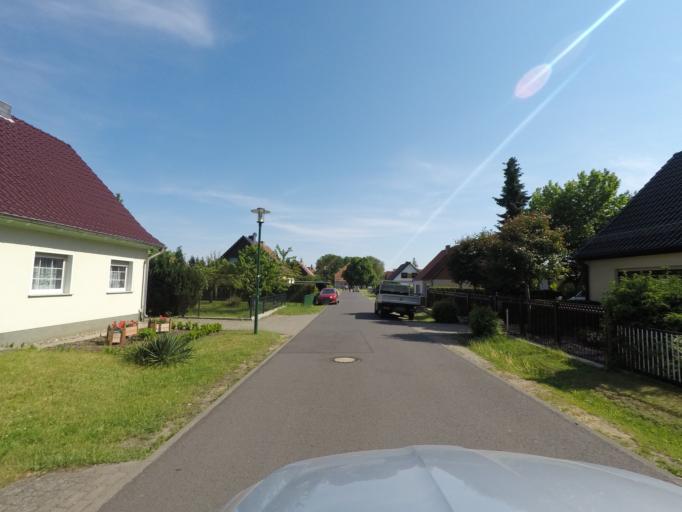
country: DE
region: Brandenburg
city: Melchow
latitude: 52.8648
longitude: 13.7179
